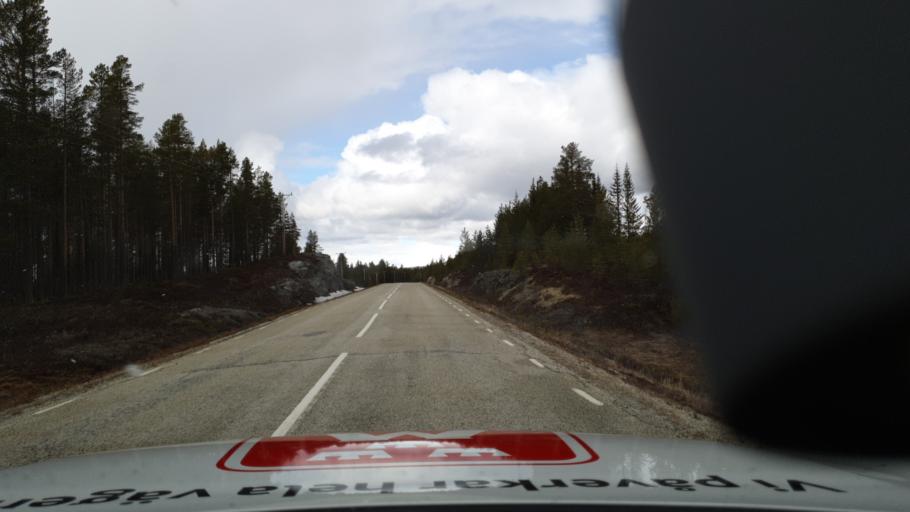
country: SE
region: Jaemtland
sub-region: Are Kommun
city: Jarpen
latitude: 62.7722
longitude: 13.7122
